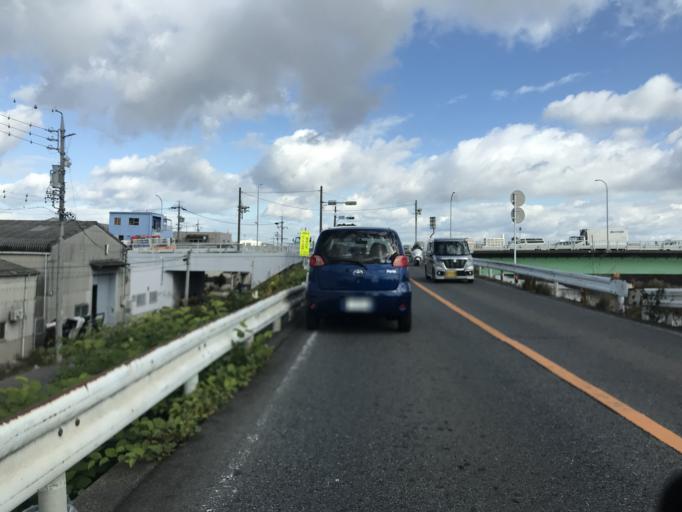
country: JP
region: Aichi
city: Nagoya-shi
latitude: 35.2150
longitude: 136.8654
